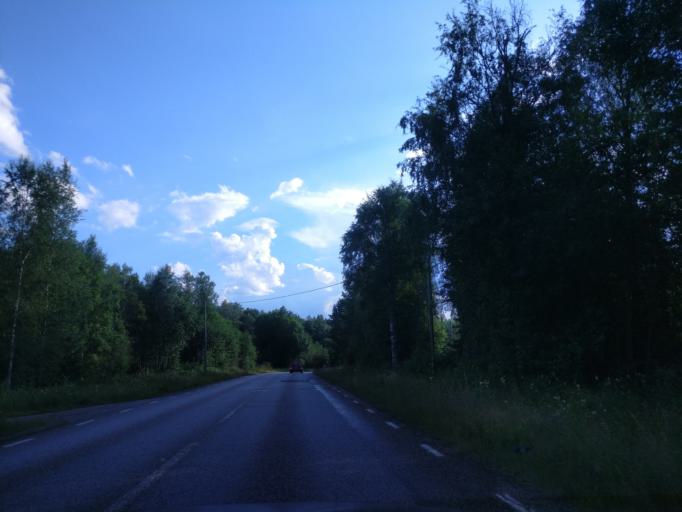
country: SE
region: Dalarna
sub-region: Ludvika Kommun
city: Ludvika
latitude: 60.2664
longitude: 15.0593
